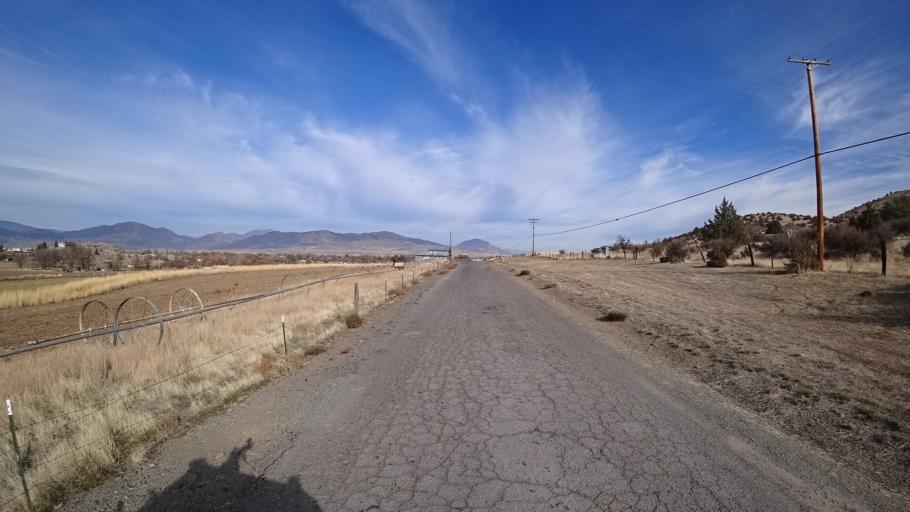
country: US
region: California
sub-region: Siskiyou County
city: Montague
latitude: 41.7171
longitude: -122.5214
